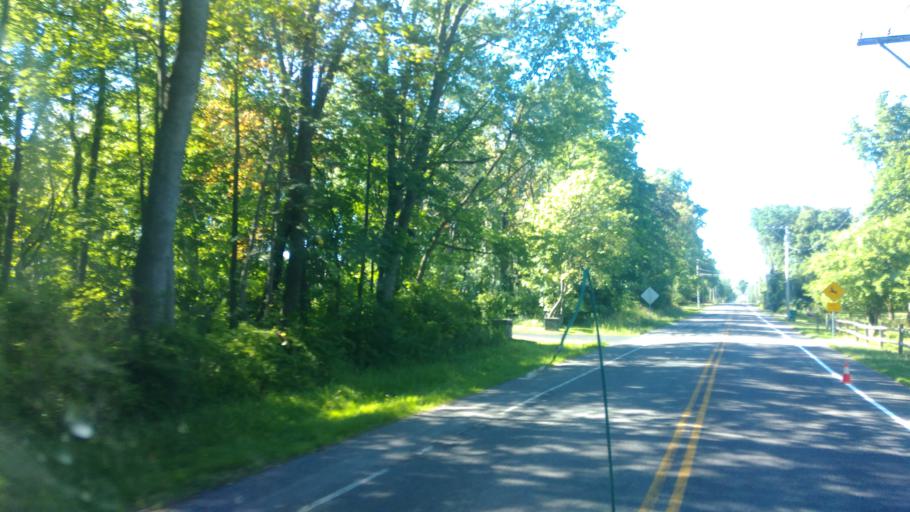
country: US
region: New York
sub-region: Monroe County
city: Webster
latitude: 43.2556
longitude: -77.4686
